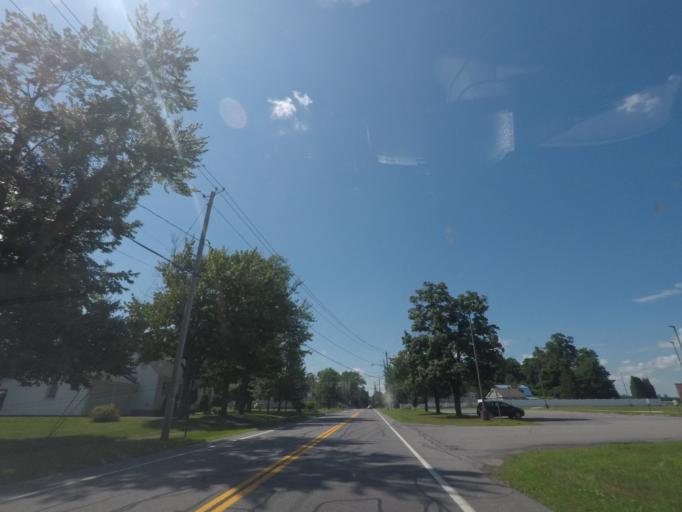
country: US
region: New York
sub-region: Schenectady County
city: Rotterdam
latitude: 42.7948
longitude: -73.9890
